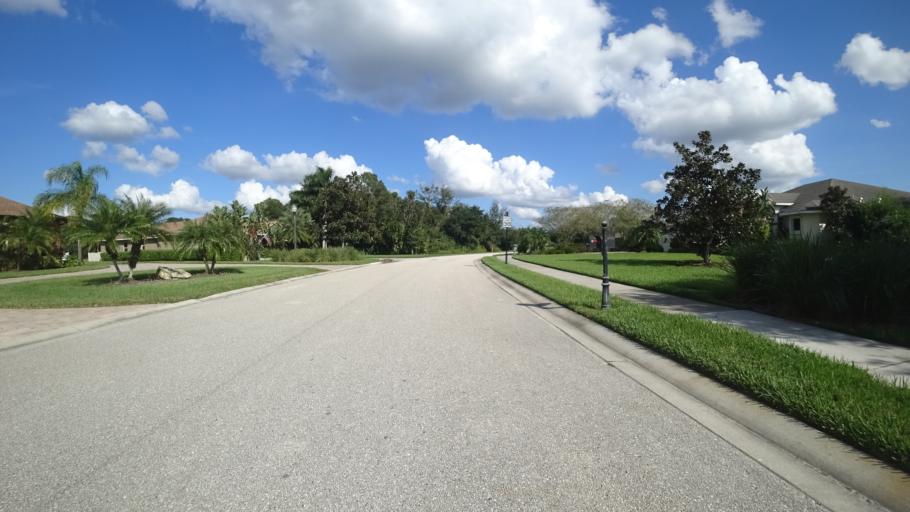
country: US
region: Florida
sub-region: Manatee County
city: Ellenton
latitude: 27.5463
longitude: -82.3874
